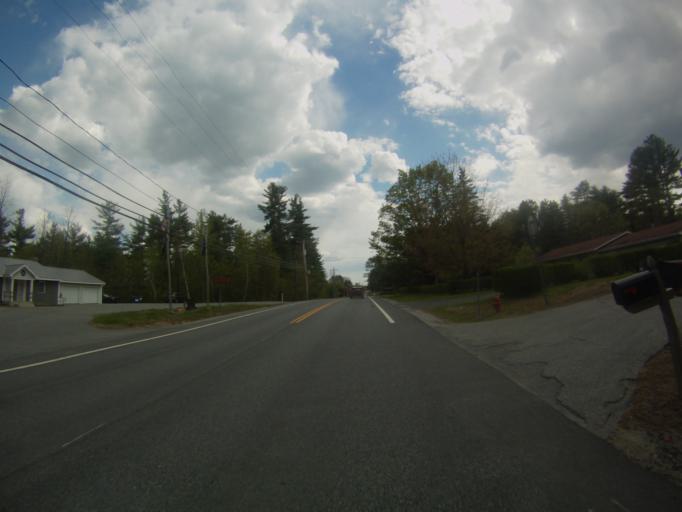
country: US
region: New York
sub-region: Essex County
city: Ticonderoga
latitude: 43.8584
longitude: -73.7558
